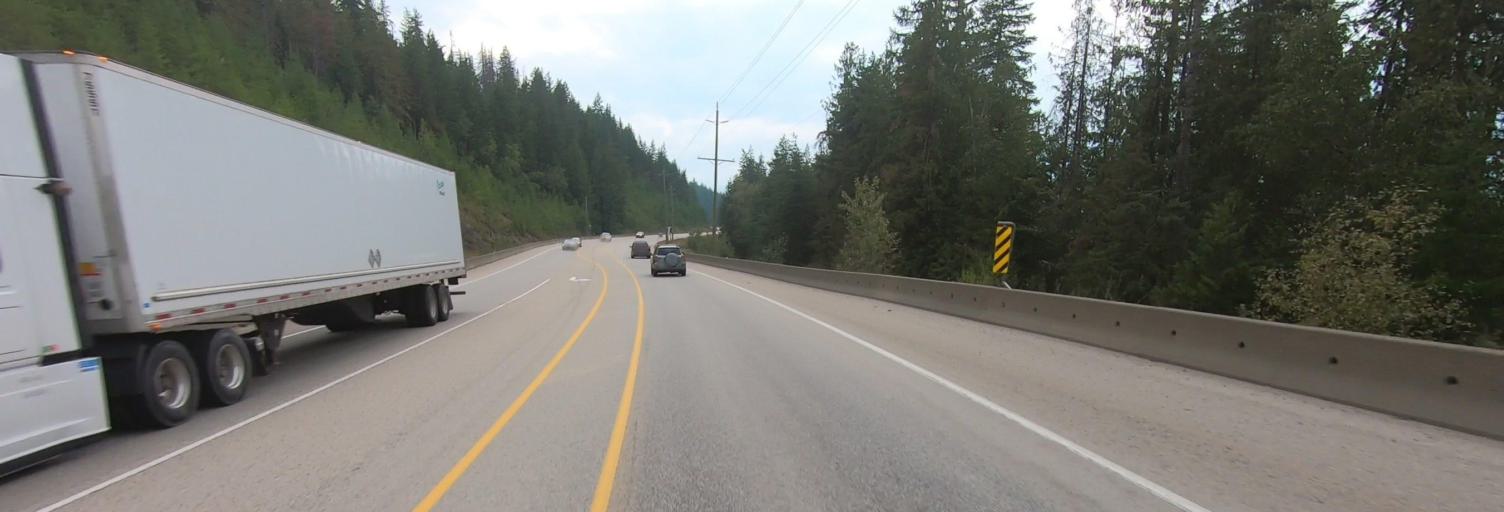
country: CA
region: British Columbia
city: Sicamous
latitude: 50.7894
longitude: -119.0899
